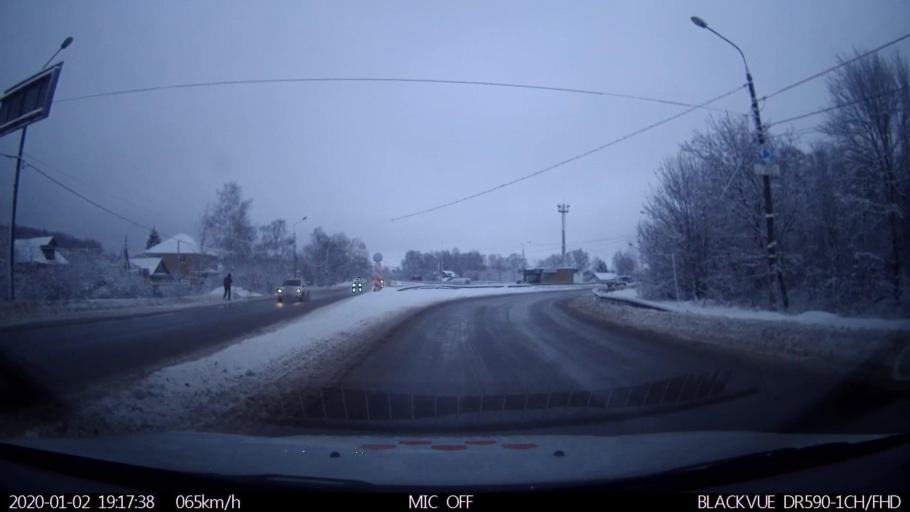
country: RU
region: Nizjnij Novgorod
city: Nizhniy Novgorod
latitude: 56.2165
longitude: 43.9271
